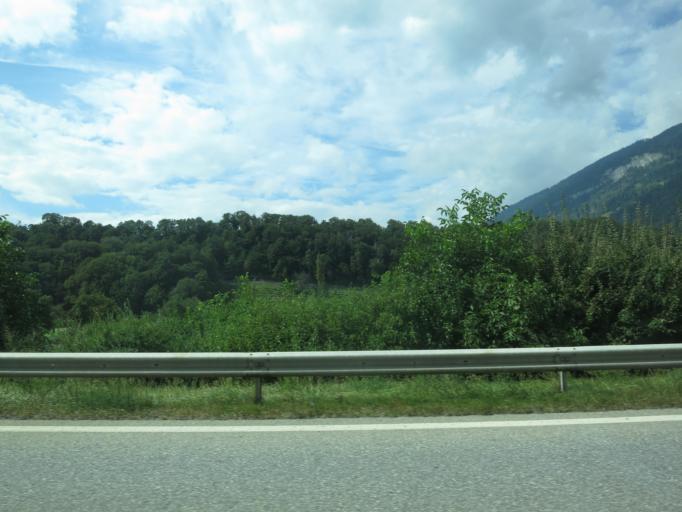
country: CH
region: Grisons
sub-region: Imboden District
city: Tamins
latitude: 46.8194
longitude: 9.4057
